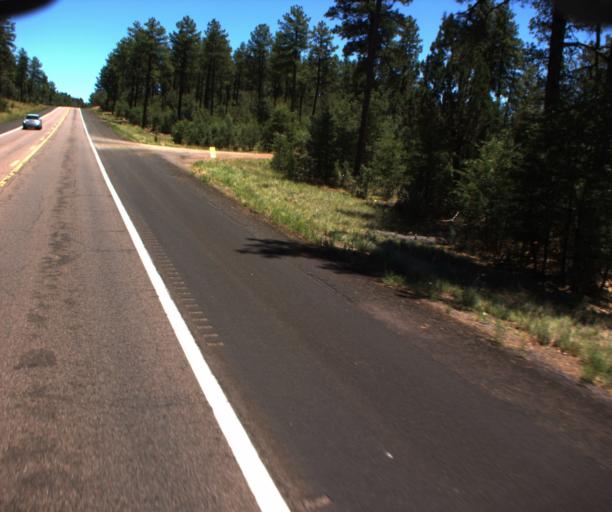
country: US
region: Arizona
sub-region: Gila County
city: Pine
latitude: 34.3693
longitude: -111.4399
